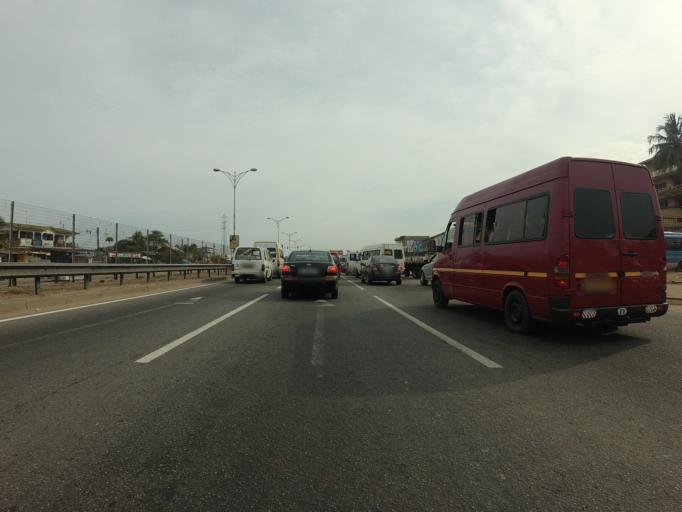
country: GH
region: Greater Accra
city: Gbawe
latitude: 5.5827
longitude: -0.2752
